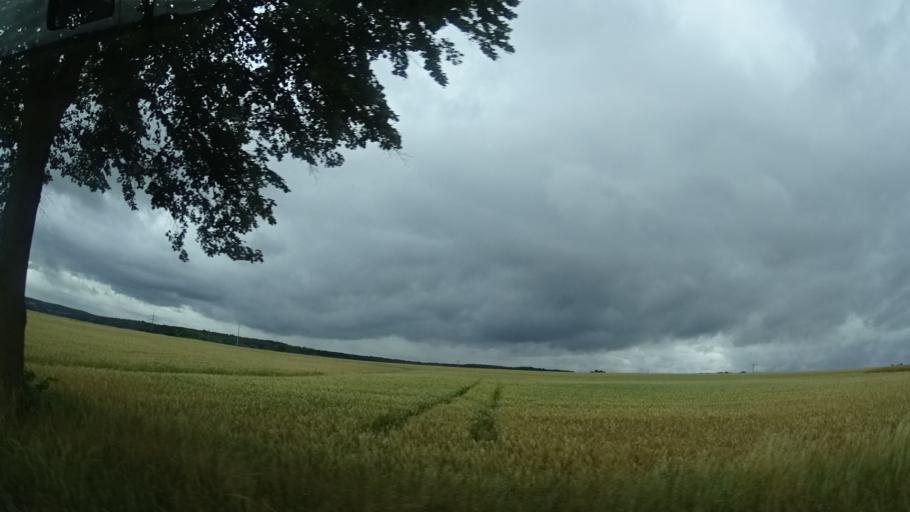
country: LU
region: Luxembourg
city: Aspelt
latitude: 49.5272
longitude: 6.2358
